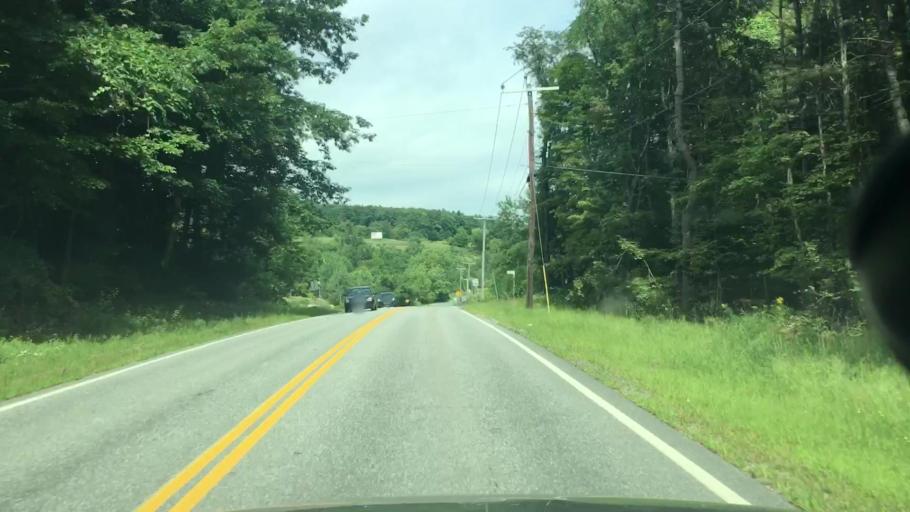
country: US
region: Massachusetts
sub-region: Franklin County
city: Colrain
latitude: 42.6402
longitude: -72.6714
